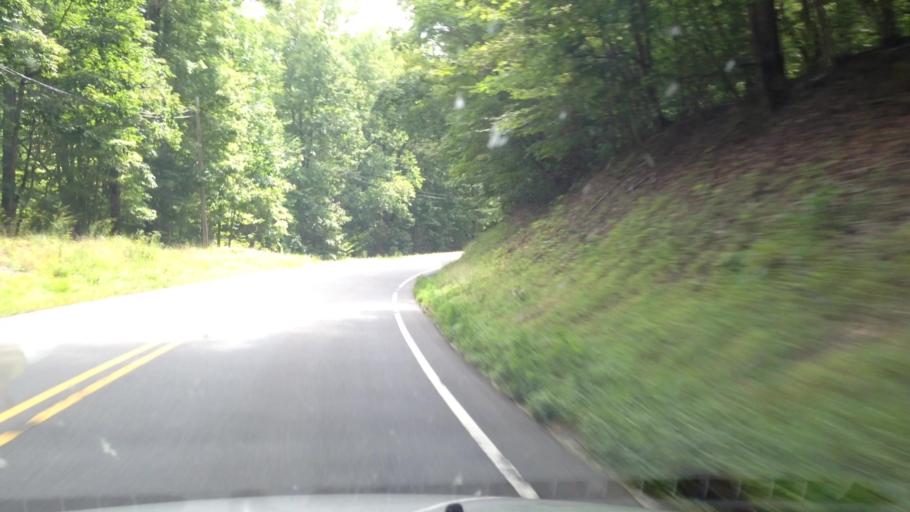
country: US
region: North Carolina
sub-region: Rockingham County
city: Wentworth
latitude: 36.3970
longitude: -79.8023
